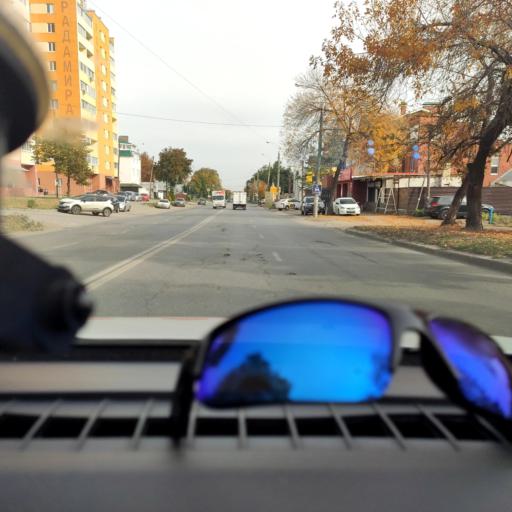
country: RU
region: Samara
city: Samara
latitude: 53.1863
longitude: 50.2046
